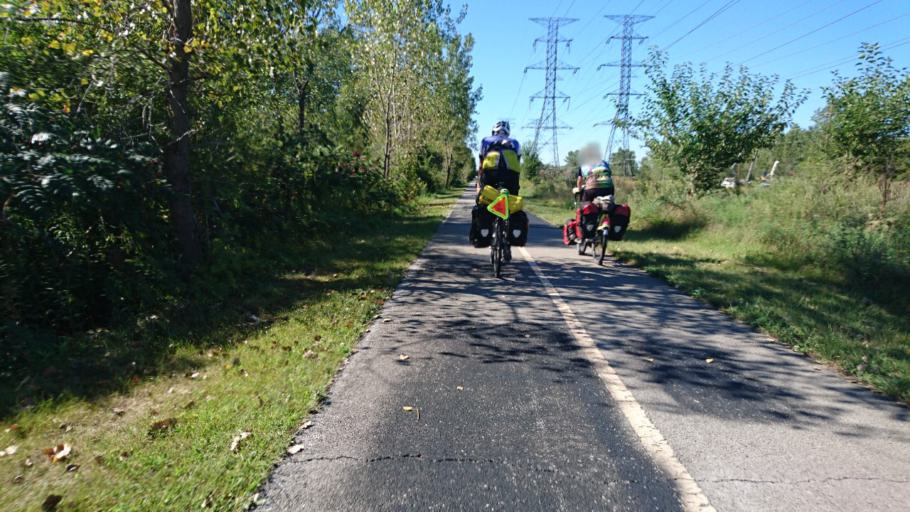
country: US
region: Indiana
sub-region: Lake County
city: Whiting
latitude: 41.6803
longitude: -87.5324
